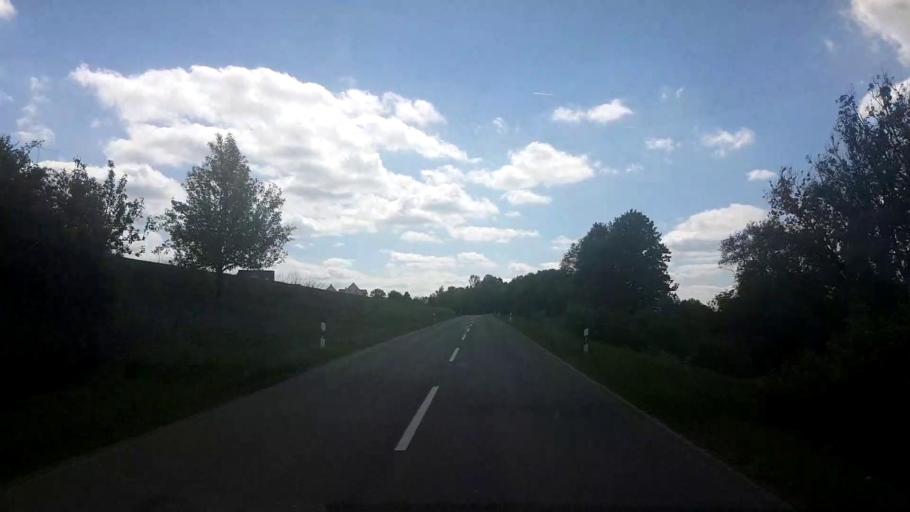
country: DE
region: Bavaria
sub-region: Upper Franconia
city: Grossheirath
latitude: 50.1696
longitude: 10.9412
